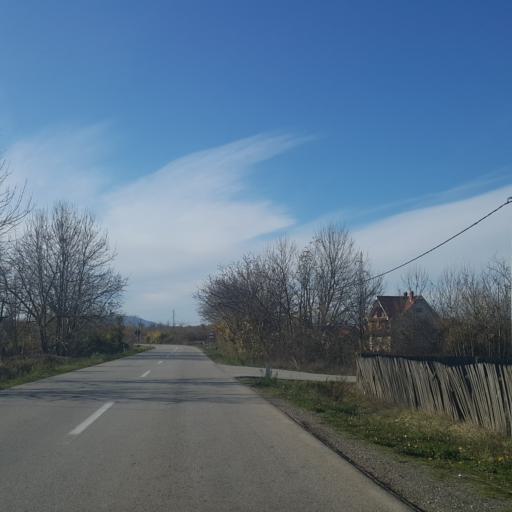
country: RS
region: Central Serbia
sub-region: Sumadijski Okrug
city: Topola
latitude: 44.2513
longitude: 20.7690
